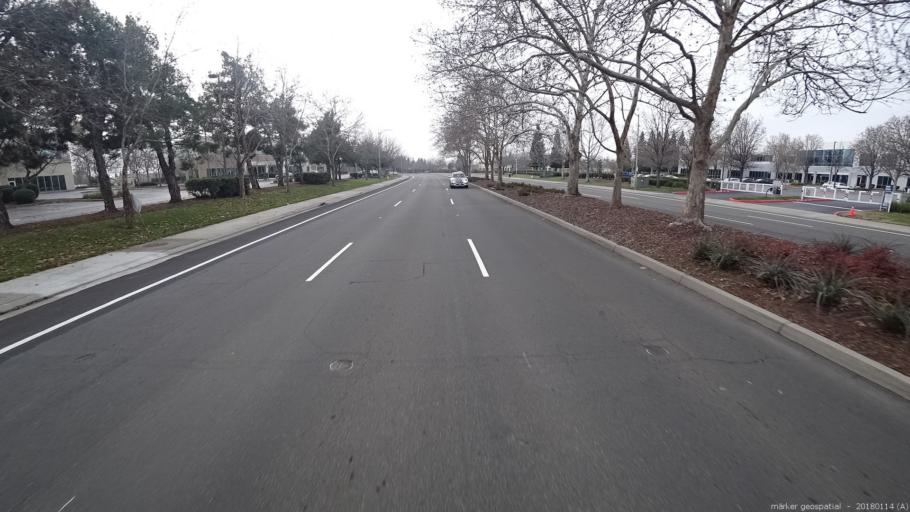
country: US
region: California
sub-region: Sacramento County
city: Rancho Cordova
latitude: 38.5811
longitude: -121.2860
